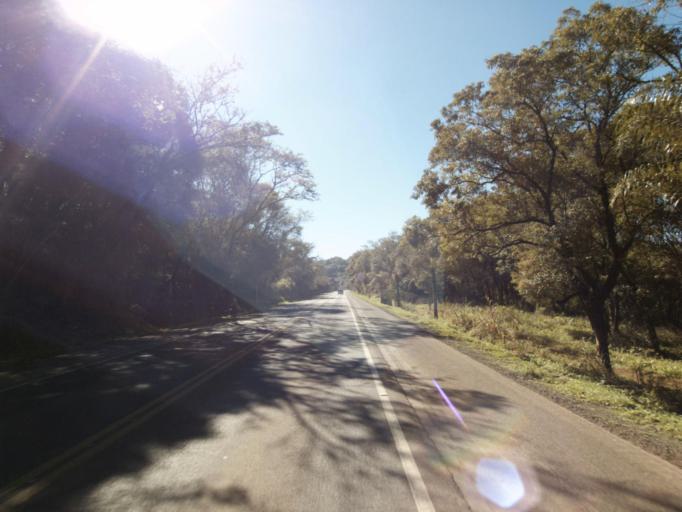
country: BR
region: Santa Catarina
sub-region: Sao Lourenco Do Oeste
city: Sao Lourenco dOeste
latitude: -26.8266
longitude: -53.1074
